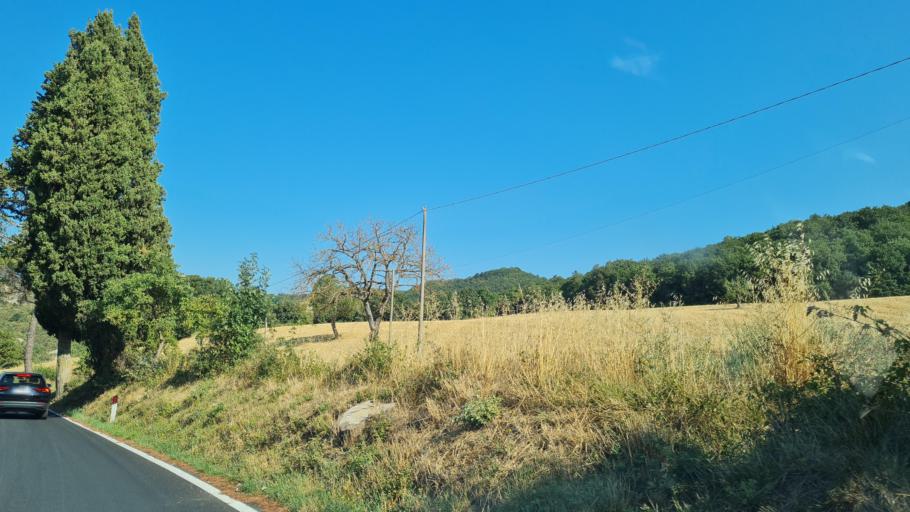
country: IT
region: Tuscany
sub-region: Provincia di Siena
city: Chianciano Terme
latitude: 43.0296
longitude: 11.7739
